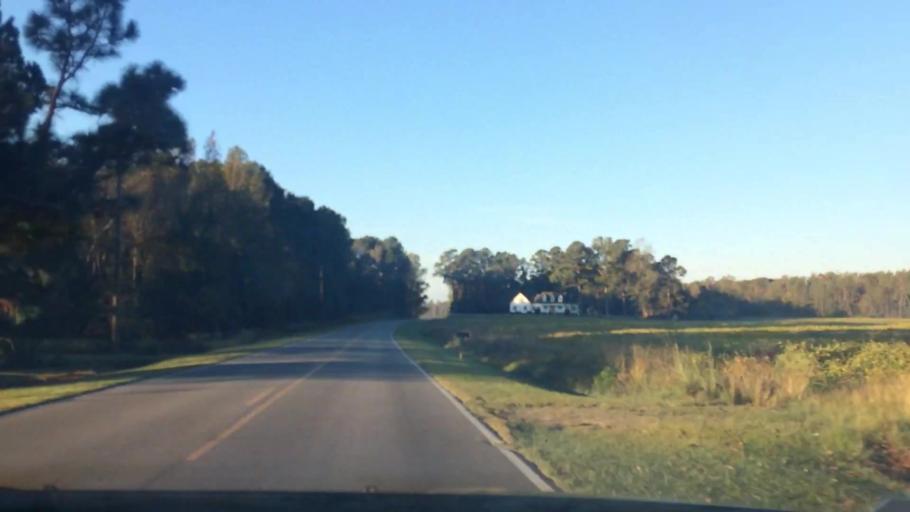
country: US
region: North Carolina
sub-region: Pitt County
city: Grifton
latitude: 35.3864
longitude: -77.4069
